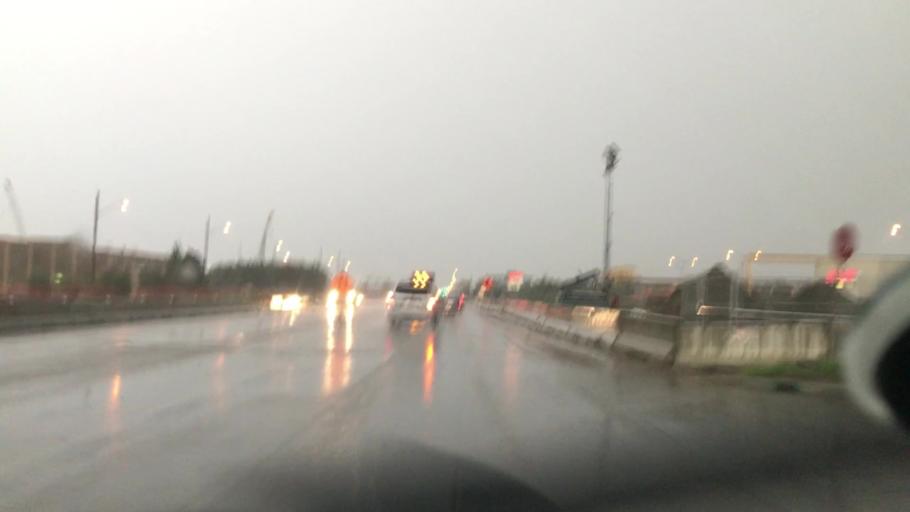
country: CA
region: Alberta
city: Edmonton
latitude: 53.4950
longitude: -113.4426
